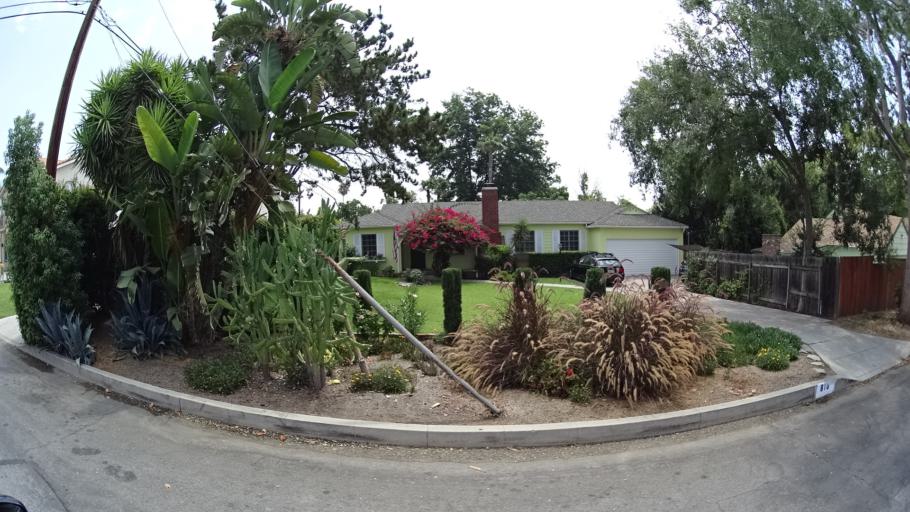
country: US
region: California
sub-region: Los Angeles County
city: Burbank
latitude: 34.1824
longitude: -118.2931
